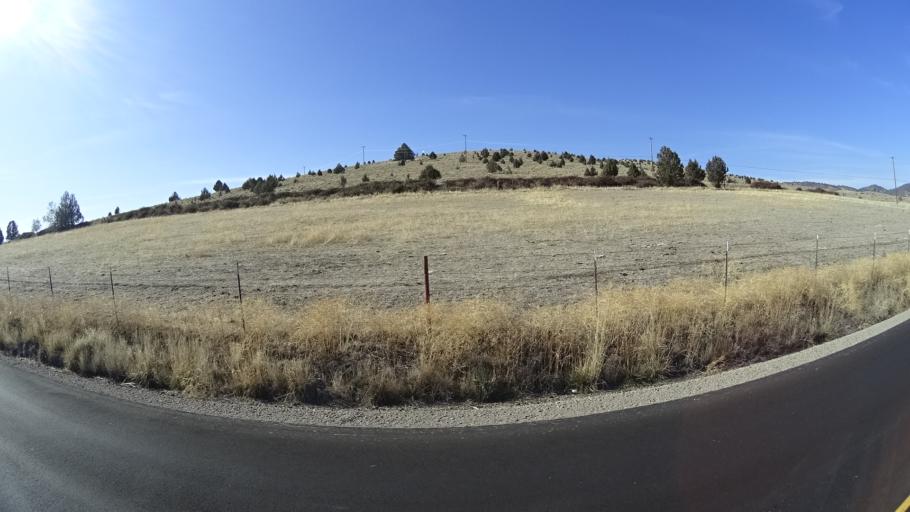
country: US
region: California
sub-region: Siskiyou County
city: Montague
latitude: 41.6024
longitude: -122.5307
